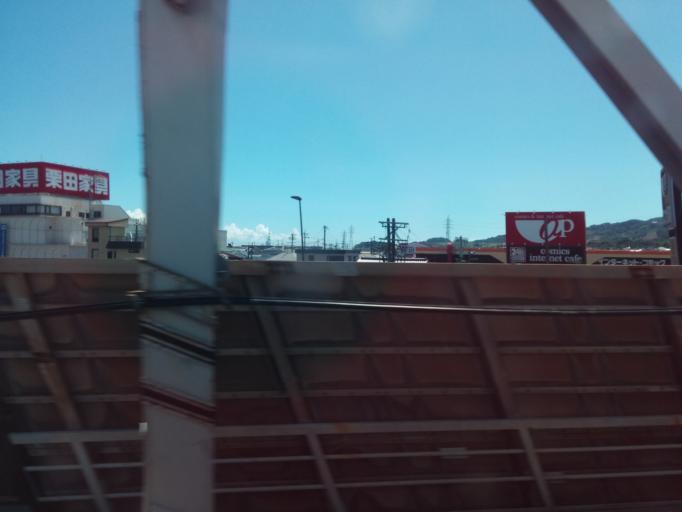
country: JP
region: Shizuoka
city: Shizuoka-shi
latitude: 35.0163
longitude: 138.4610
